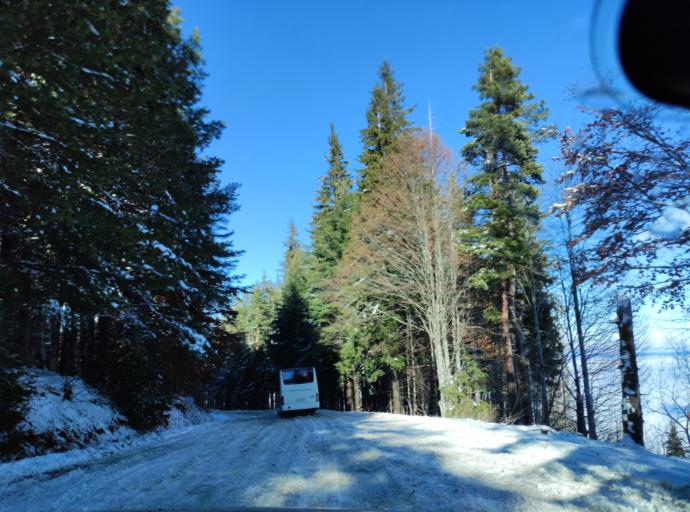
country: BG
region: Sofia-Capital
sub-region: Stolichna Obshtina
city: Sofia
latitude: 42.5925
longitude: 23.3124
